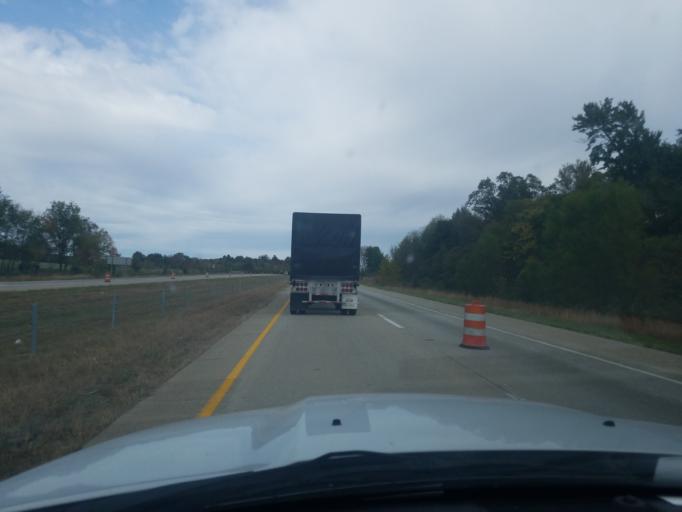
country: US
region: Indiana
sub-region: Gibson County
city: Haubstadt
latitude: 38.1599
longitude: -87.4725
